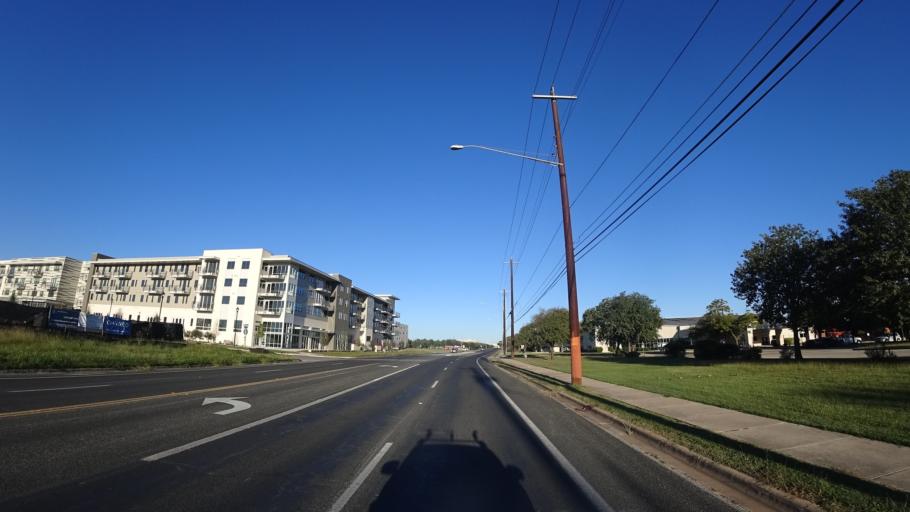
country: US
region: Texas
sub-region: Travis County
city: Austin
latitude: 30.3047
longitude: -97.7003
